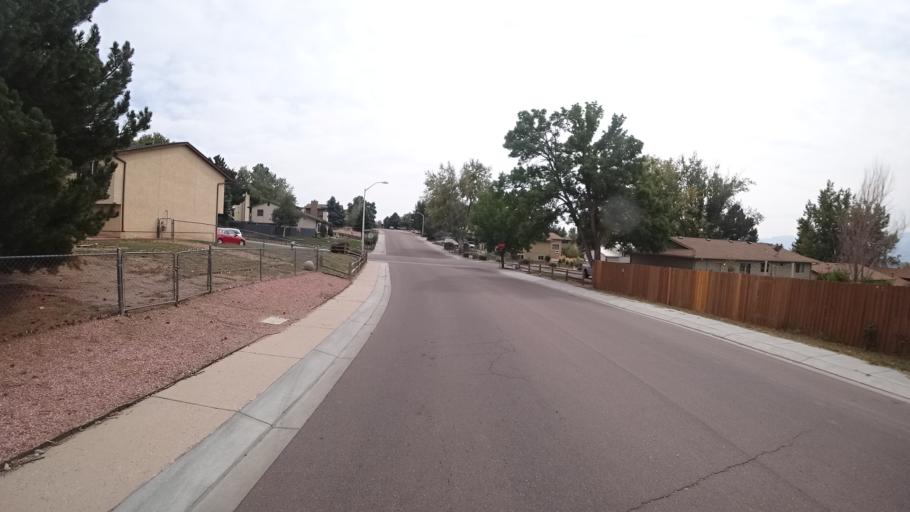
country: US
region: Colorado
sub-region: El Paso County
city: Cimarron Hills
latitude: 38.8945
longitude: -104.7345
